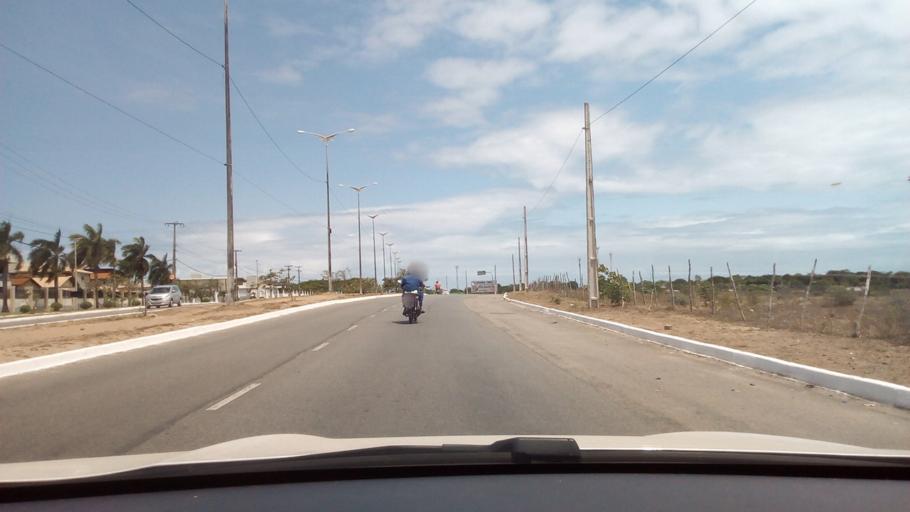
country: BR
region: Paraiba
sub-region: Joao Pessoa
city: Joao Pessoa
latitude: -7.1609
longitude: -34.8063
